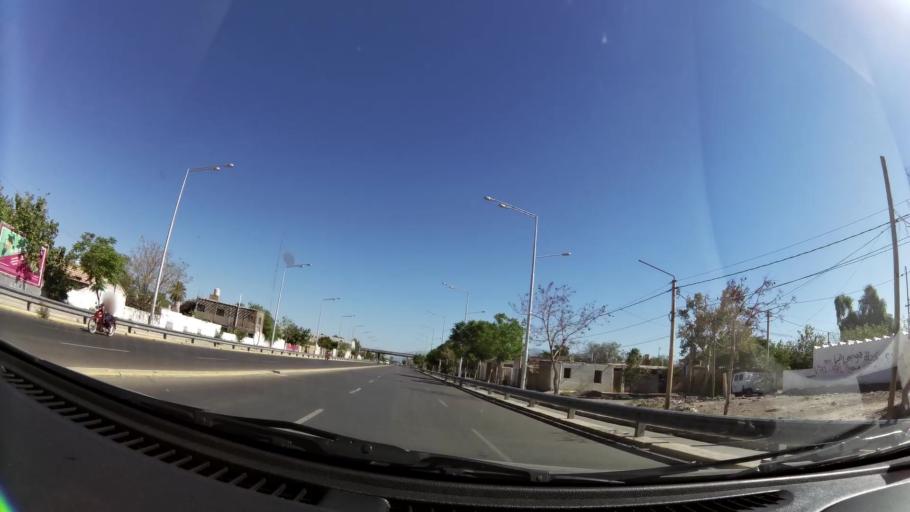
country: AR
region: San Juan
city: San Juan
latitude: -31.5514
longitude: -68.5382
